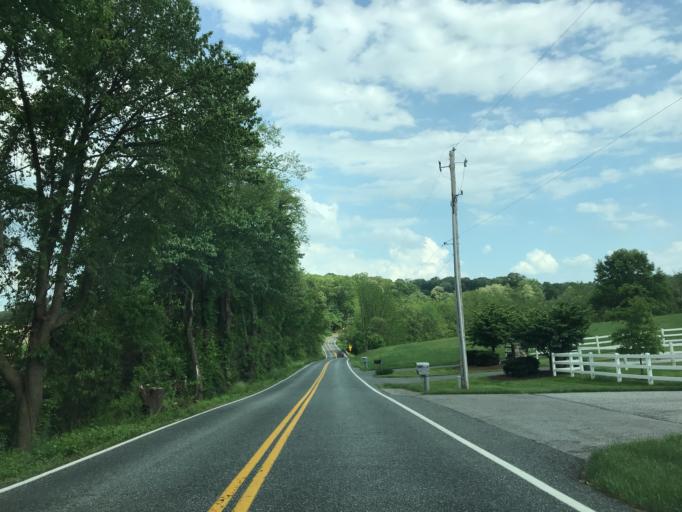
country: US
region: Pennsylvania
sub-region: York County
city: Susquehanna Trails
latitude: 39.6755
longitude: -76.3861
